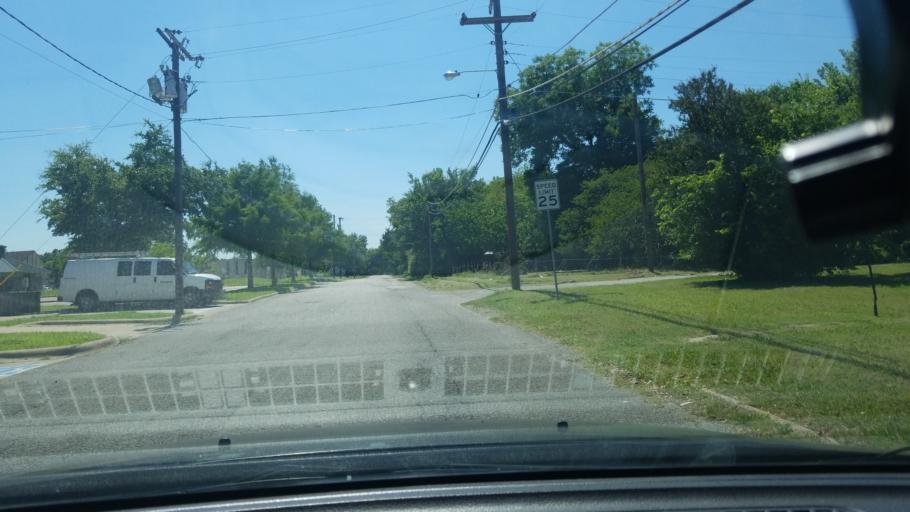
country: US
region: Texas
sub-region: Dallas County
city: Mesquite
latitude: 32.7641
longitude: -96.5993
